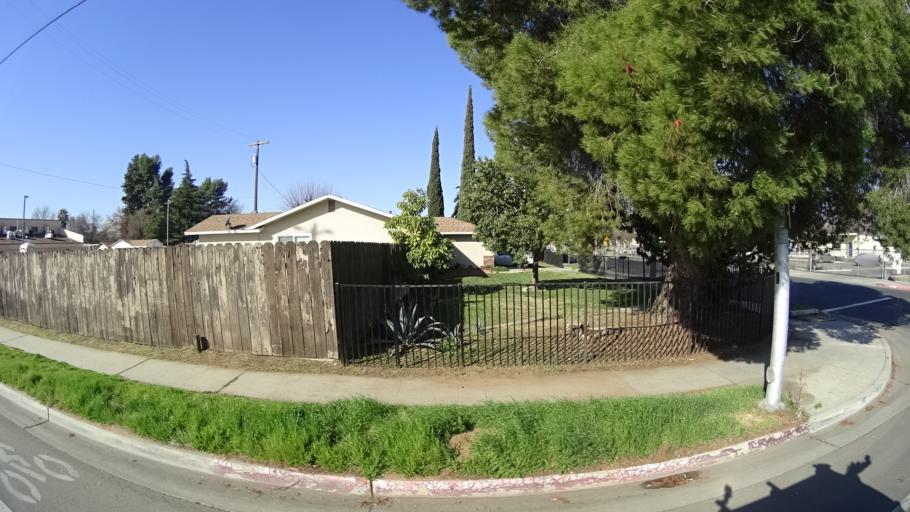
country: US
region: California
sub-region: Fresno County
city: Fresno
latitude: 36.7122
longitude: -119.7368
